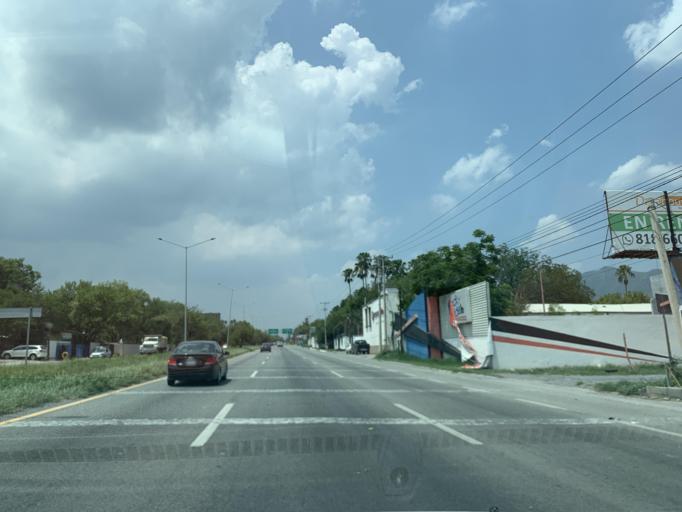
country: MX
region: Nuevo Leon
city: Santiago
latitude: 25.4650
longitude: -100.1724
